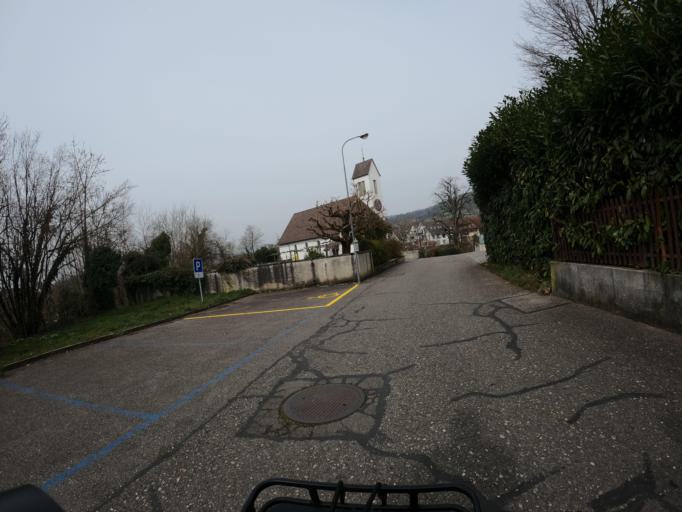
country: CH
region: Aargau
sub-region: Bezirk Lenzburg
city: Niederlenz
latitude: 47.4139
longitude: 8.1813
